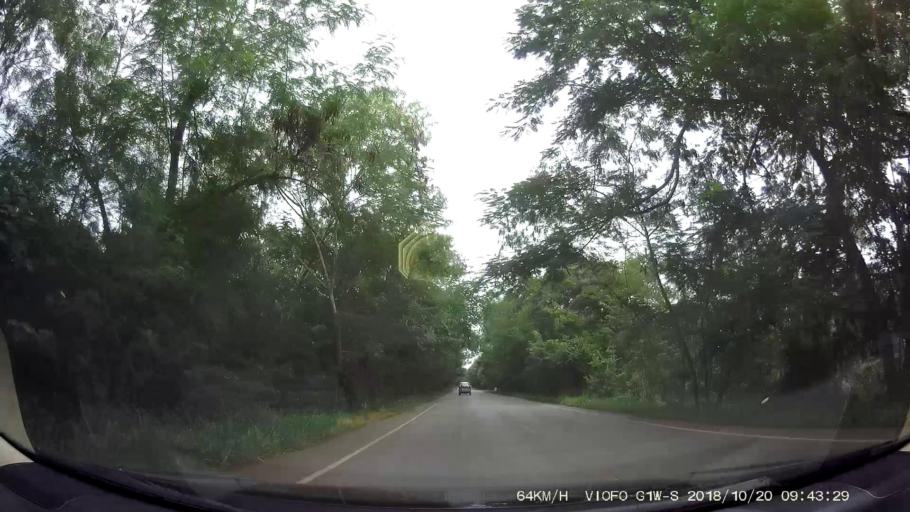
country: TH
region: Chaiyaphum
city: Khon San
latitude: 16.4740
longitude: 101.9479
